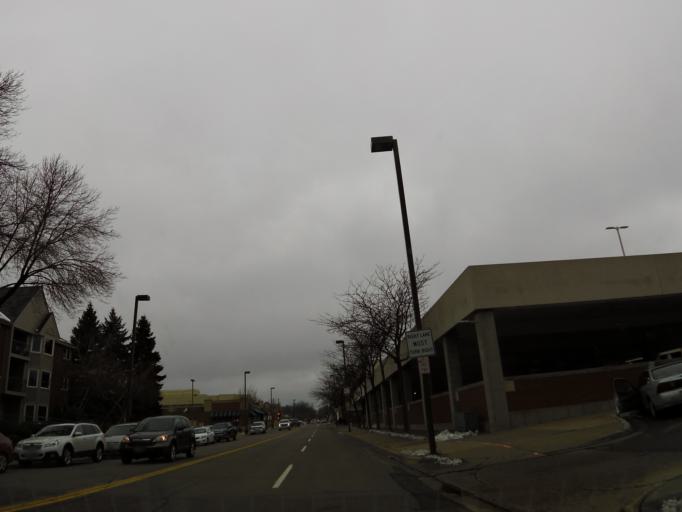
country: US
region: Minnesota
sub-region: Hennepin County
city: Minnetonka Mills
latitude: 44.9228
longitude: -93.4140
